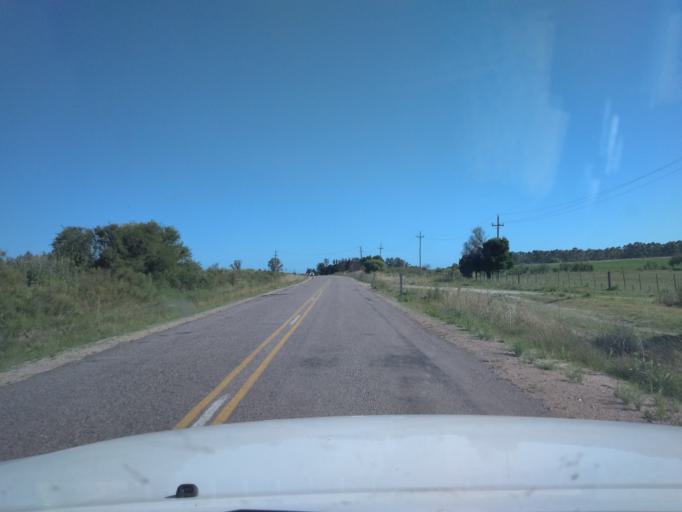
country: UY
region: Canelones
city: San Ramon
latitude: -34.2613
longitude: -55.9273
